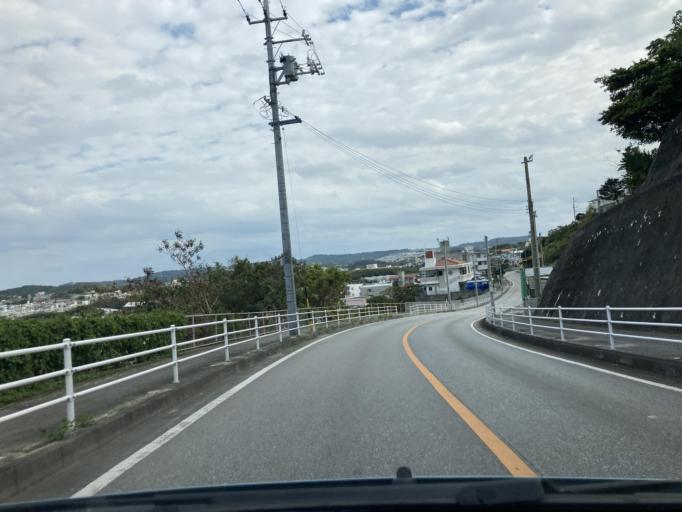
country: JP
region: Okinawa
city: Tomigusuku
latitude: 26.1801
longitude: 127.7037
